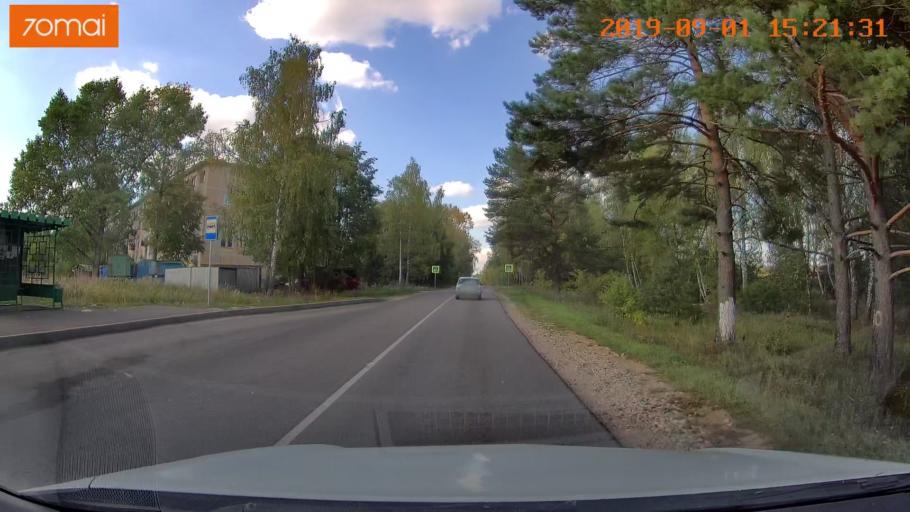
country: RU
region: Kaluga
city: Maloyaroslavets
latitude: 54.9289
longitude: 36.4720
